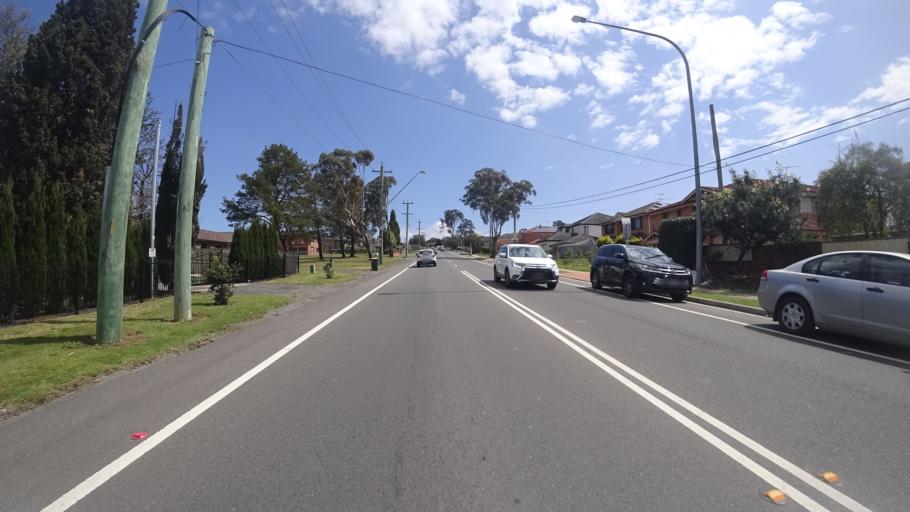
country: AU
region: New South Wales
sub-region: Campbelltown Municipality
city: Glenfield
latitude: -33.9616
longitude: 150.8973
